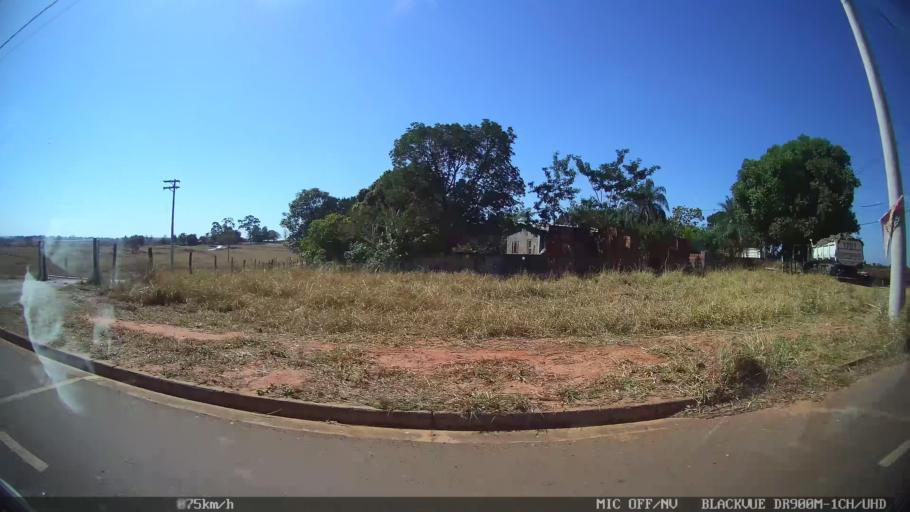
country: BR
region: Sao Paulo
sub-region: Sao Jose Do Rio Preto
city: Sao Jose do Rio Preto
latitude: -20.7324
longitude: -49.4365
